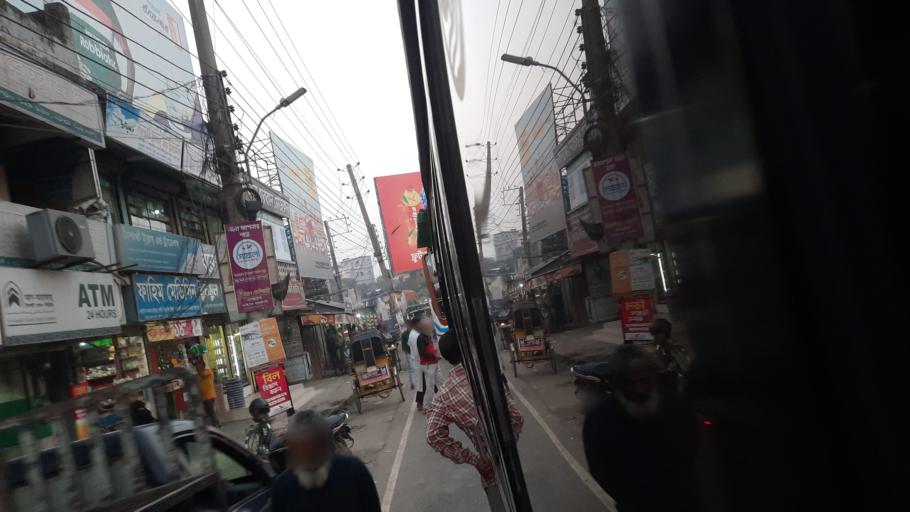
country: BD
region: Khulna
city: Jessore
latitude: 23.1809
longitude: 89.1911
